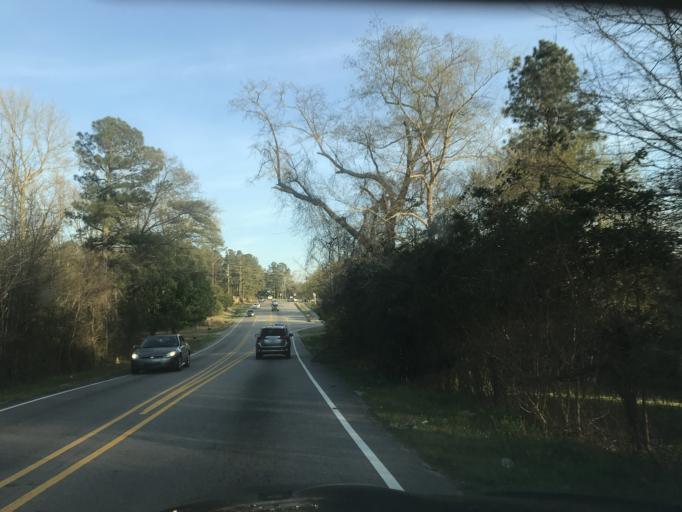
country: US
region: North Carolina
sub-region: Wake County
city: Garner
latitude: 35.7335
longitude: -78.5607
